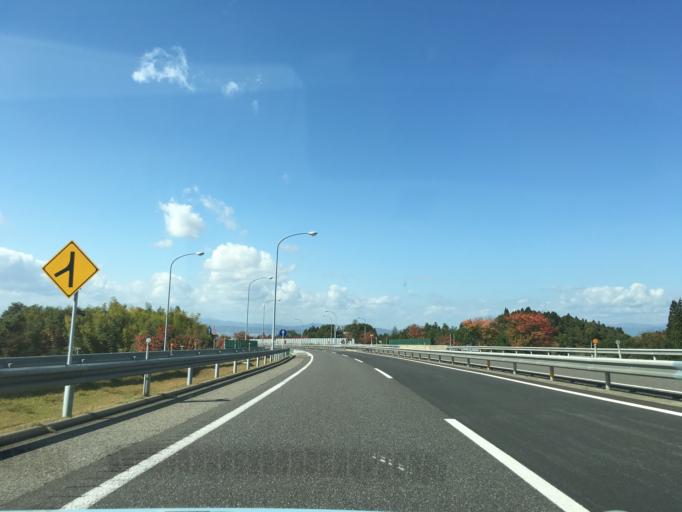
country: JP
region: Fukushima
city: Kitakata
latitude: 37.5507
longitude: 139.9717
